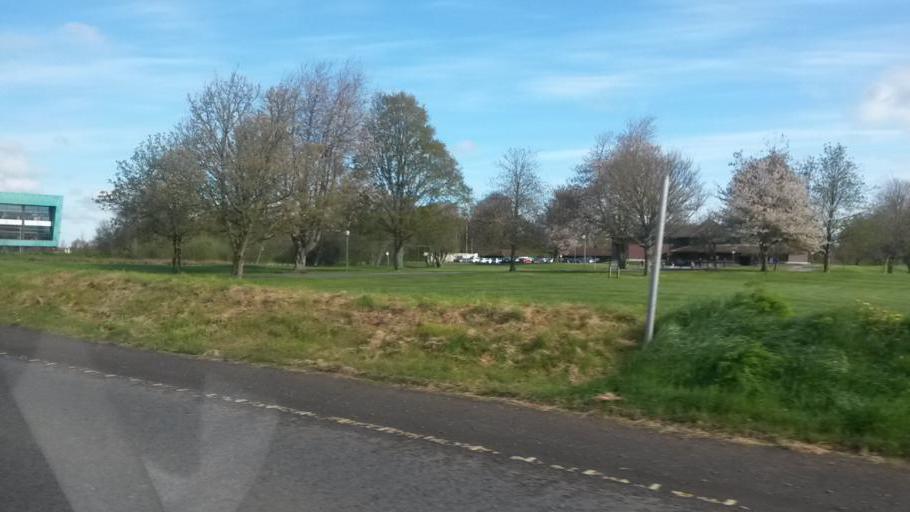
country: IE
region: Leinster
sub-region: An Mhi
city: Kells
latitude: 53.7237
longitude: -6.8603
